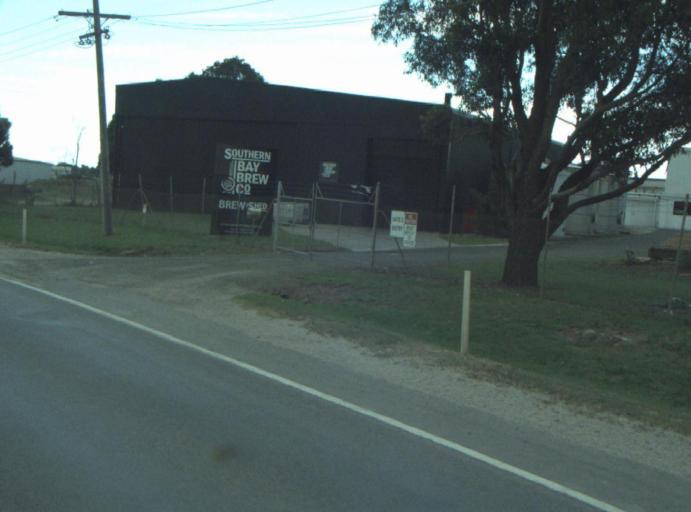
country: AU
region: Victoria
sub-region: Greater Geelong
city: Leopold
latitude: -38.1618
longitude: 144.4289
